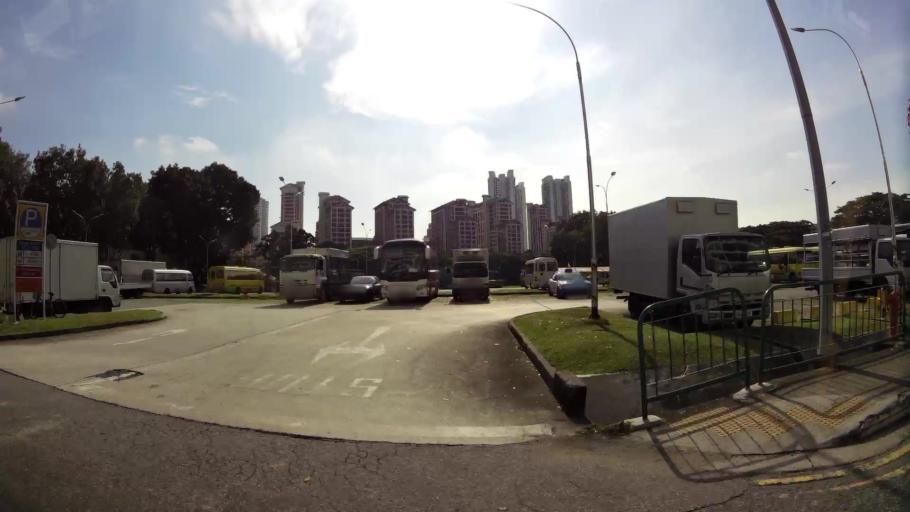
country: SG
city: Singapore
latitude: 1.3590
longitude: 103.8396
